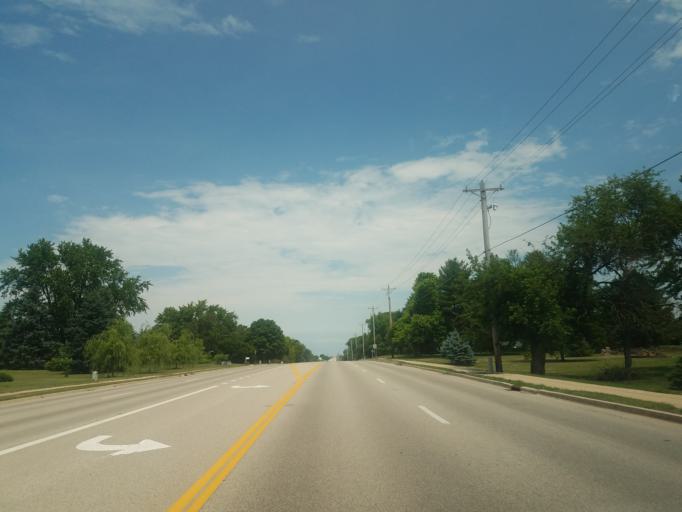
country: US
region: Illinois
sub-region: McLean County
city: Downs
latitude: 40.4216
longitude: -88.9013
